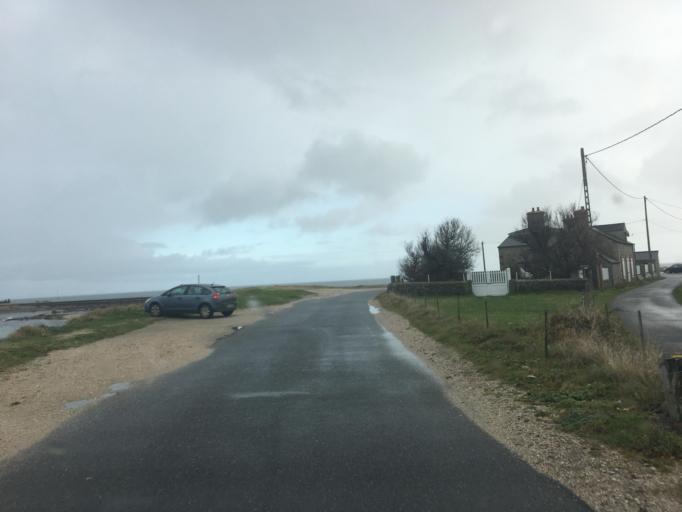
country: FR
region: Lower Normandy
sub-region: Departement de la Manche
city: Reville
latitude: 49.6950
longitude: -1.2689
